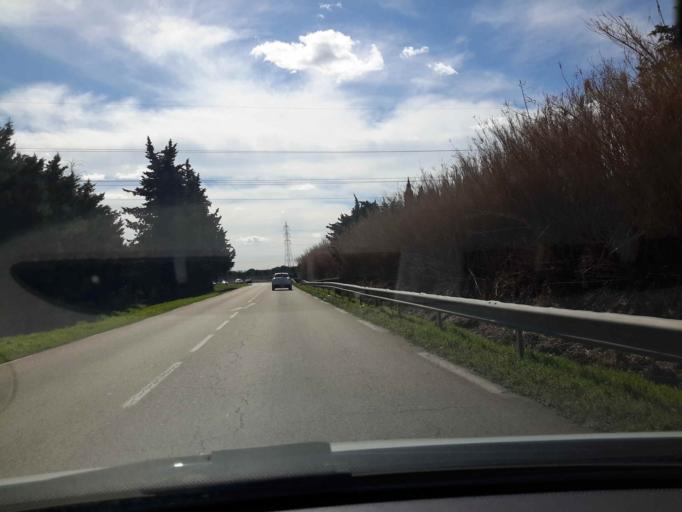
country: FR
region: Languedoc-Roussillon
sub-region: Departement du Gard
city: Caissargues
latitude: 43.8031
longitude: 4.3541
